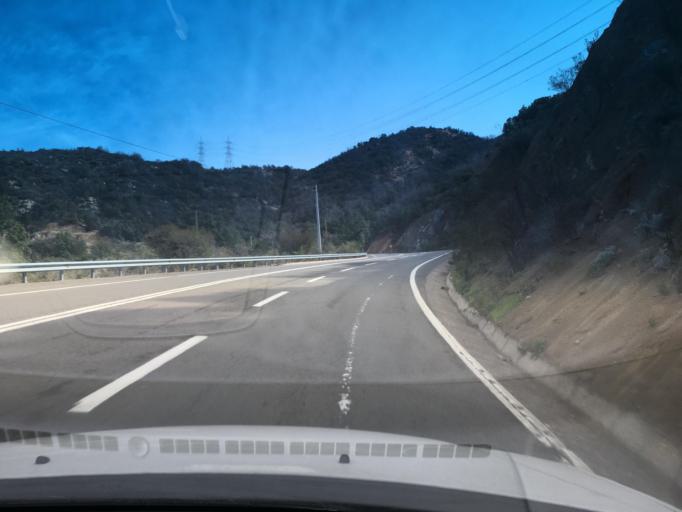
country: CL
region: Valparaiso
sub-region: Provincia de San Felipe
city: Llaillay
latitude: -33.0582
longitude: -71.0016
